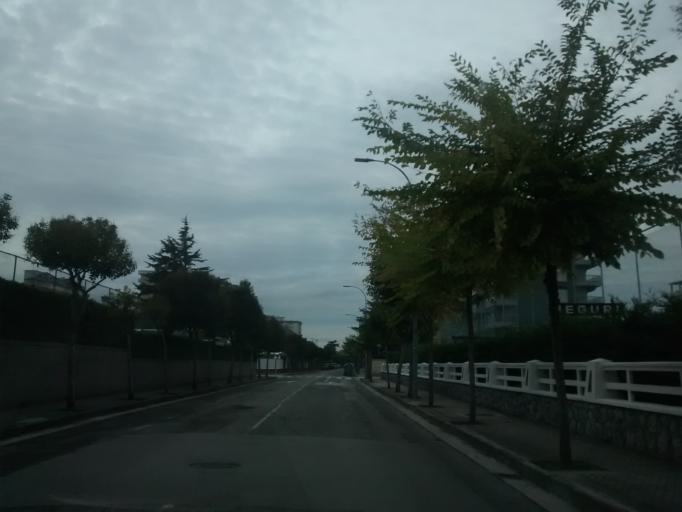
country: ES
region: Cantabria
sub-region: Provincia de Cantabria
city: Laredo
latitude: 43.4110
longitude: -3.4320
